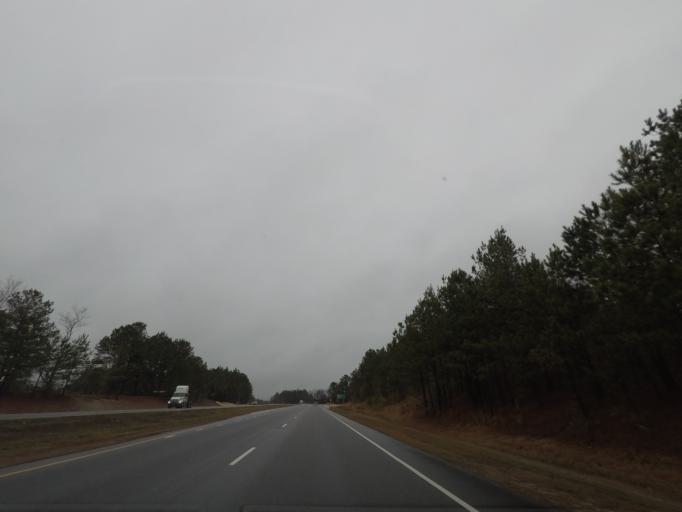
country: US
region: North Carolina
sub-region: Lee County
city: Broadway
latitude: 35.3306
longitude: -79.0940
